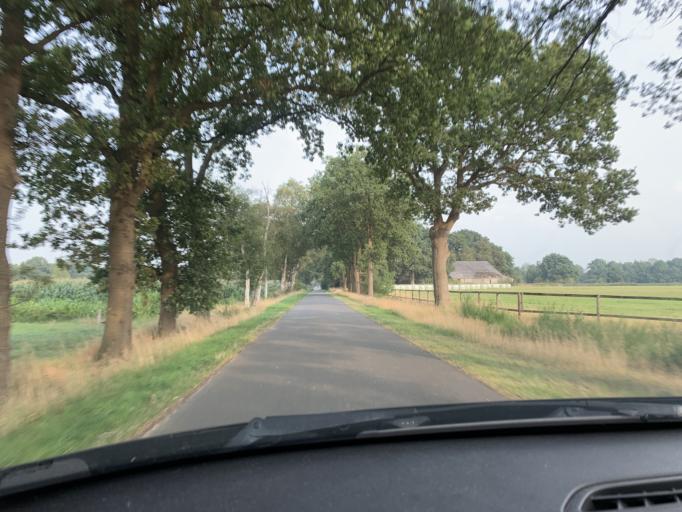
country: DE
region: Lower Saxony
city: Westerstede
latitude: 53.2595
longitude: 7.8812
